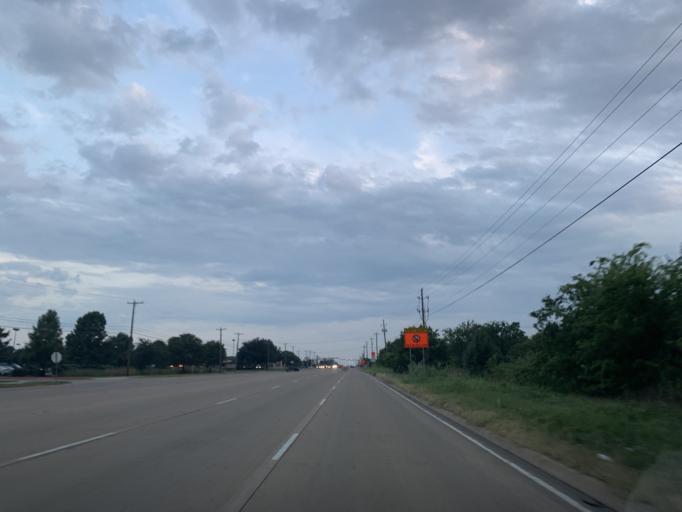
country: US
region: Texas
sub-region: Tarrant County
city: Keller
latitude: 32.8985
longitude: -97.2582
